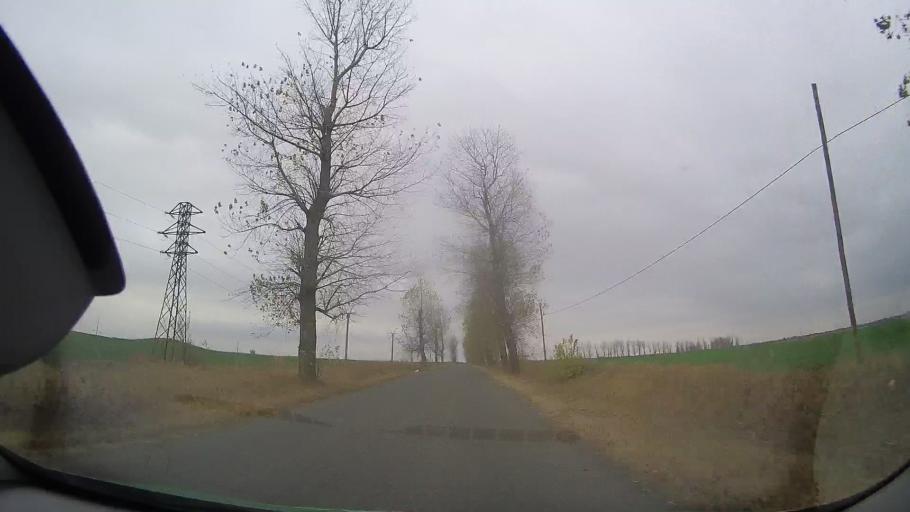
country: RO
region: Buzau
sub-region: Comuna Rusetu
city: Rusetu
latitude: 44.9433
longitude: 27.2374
